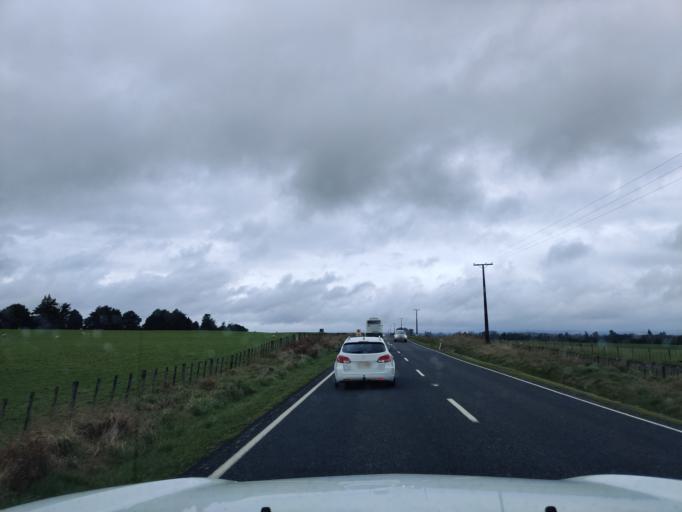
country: NZ
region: Manawatu-Wanganui
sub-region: Ruapehu District
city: Waiouru
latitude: -39.3575
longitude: 175.3516
